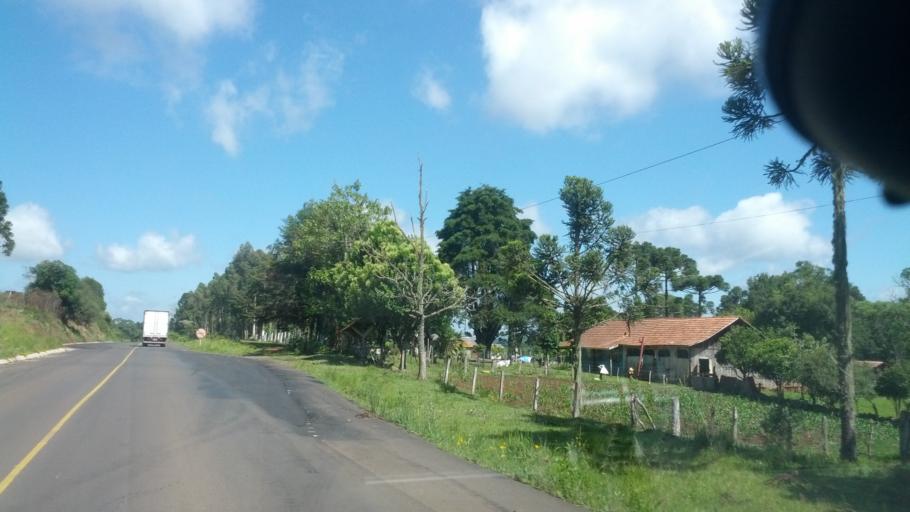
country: BR
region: Santa Catarina
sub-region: Lages
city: Lages
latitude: -27.9305
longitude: -50.5311
